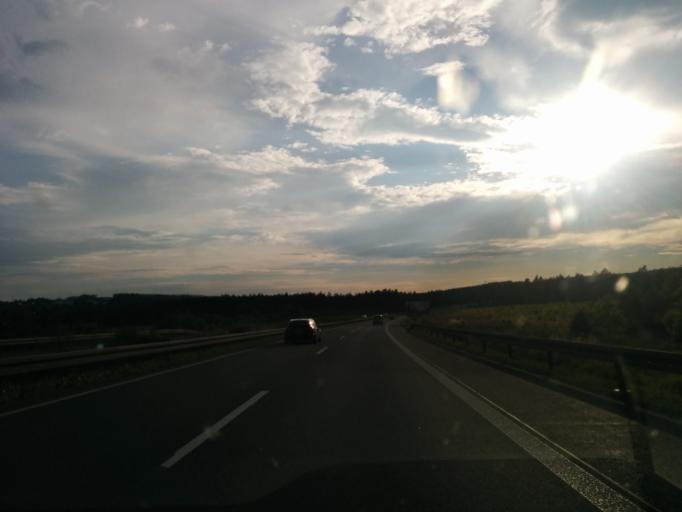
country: DE
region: Thuringia
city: Neuhaus
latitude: 50.7106
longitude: 10.9473
